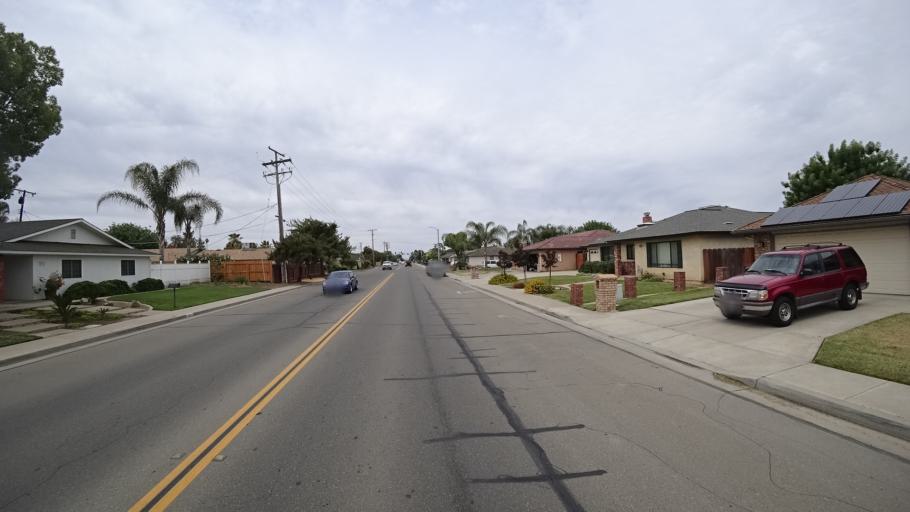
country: US
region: California
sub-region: Kings County
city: Hanford
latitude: 36.3573
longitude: -119.6434
